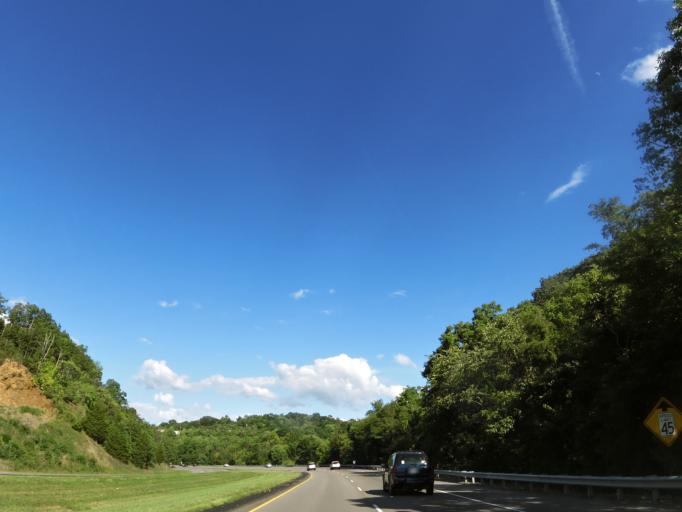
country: US
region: Tennessee
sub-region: Greene County
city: Greeneville
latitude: 36.1680
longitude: -82.8686
